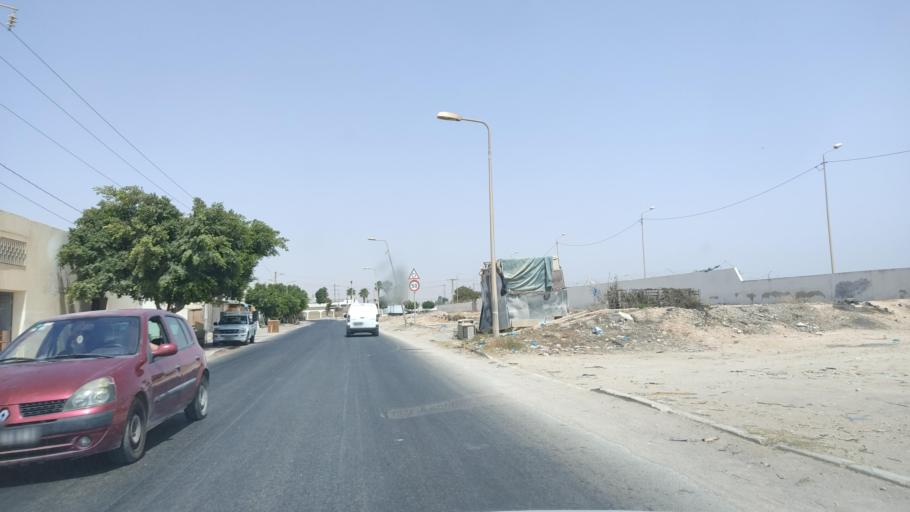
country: TN
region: Safaqis
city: Sfax
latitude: 34.6981
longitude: 10.7201
